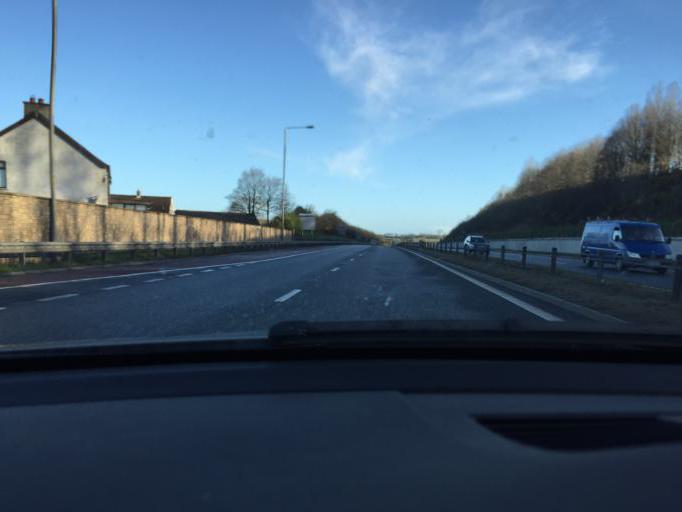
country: GB
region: Northern Ireland
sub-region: Banbridge District
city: Banbridge
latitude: 54.3131
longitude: -6.2997
